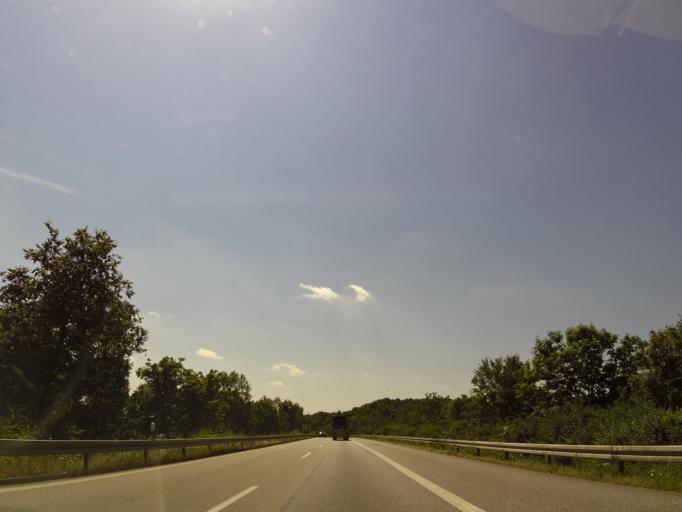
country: DE
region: Bavaria
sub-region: Upper Bavaria
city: Unterfoehring
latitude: 48.2215
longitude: 11.6320
